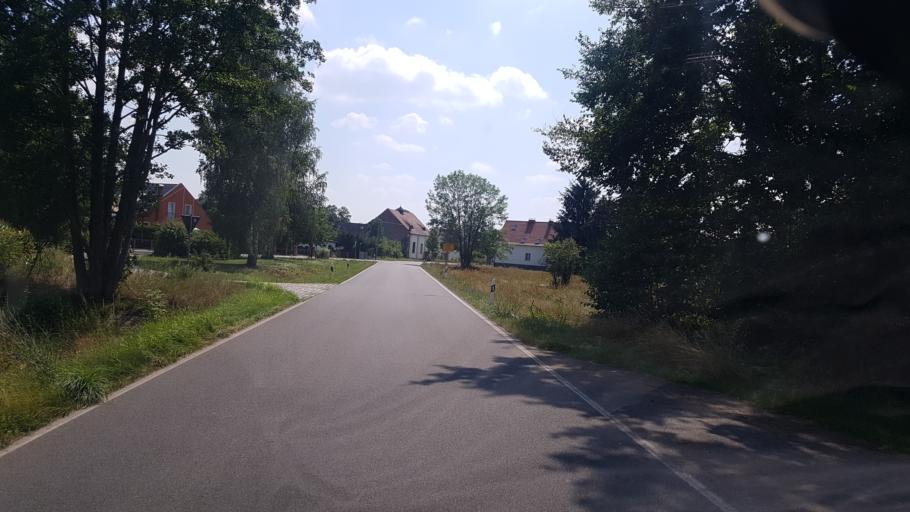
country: DE
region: Brandenburg
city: Cottbus
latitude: 51.7007
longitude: 14.4267
